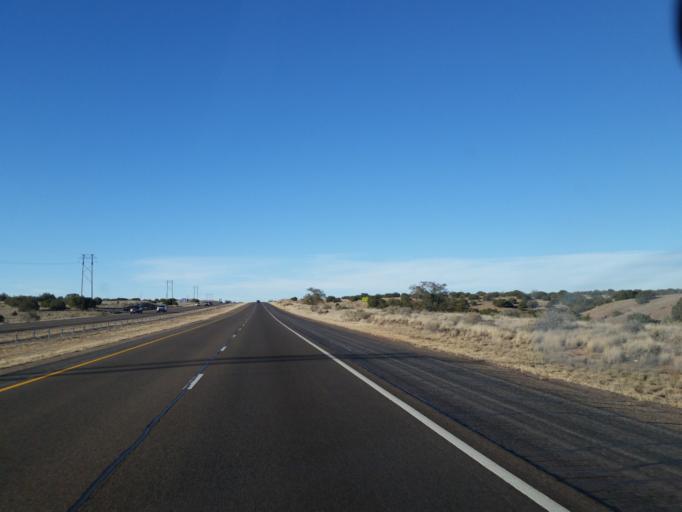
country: US
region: New Mexico
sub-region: Sandoval County
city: Santo Domingo Pueblo
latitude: 35.4769
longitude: -106.2886
